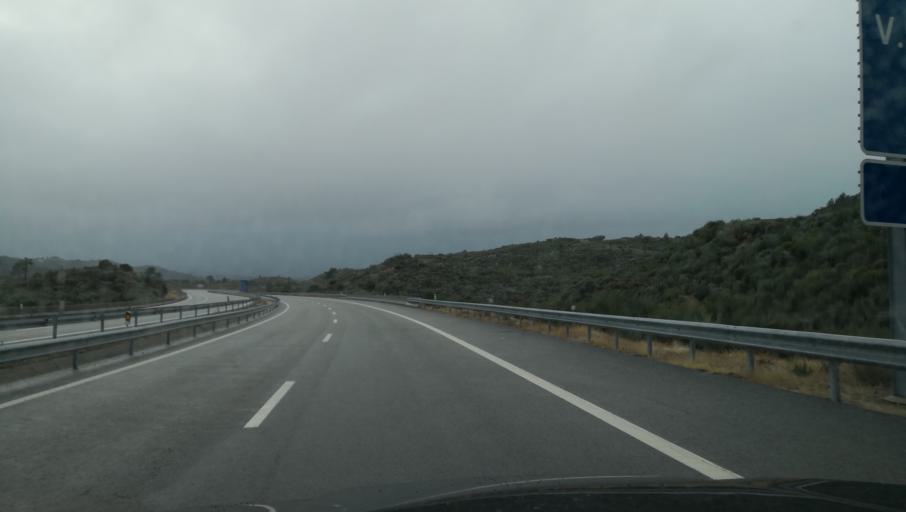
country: PT
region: Vila Real
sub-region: Vila Real
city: Vila Real
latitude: 41.3704
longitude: -7.6805
